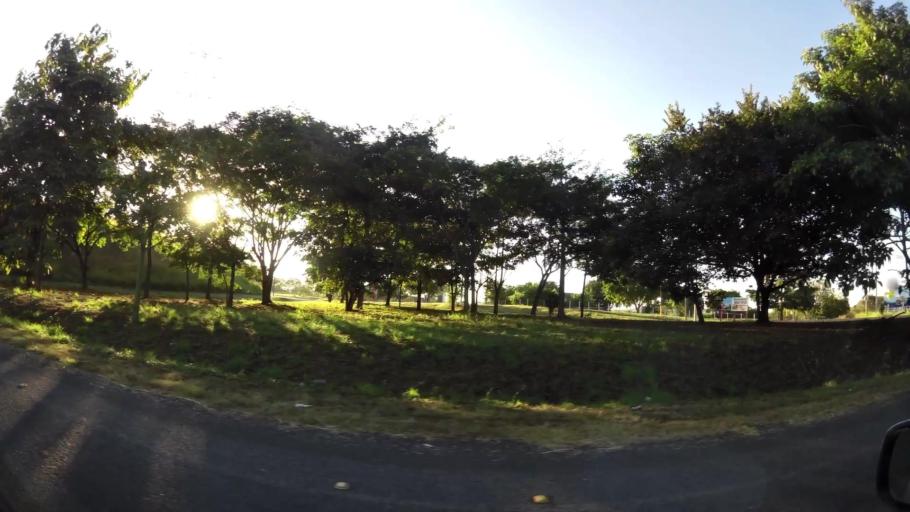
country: CR
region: Puntarenas
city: Esparza
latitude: 9.9968
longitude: -84.7152
